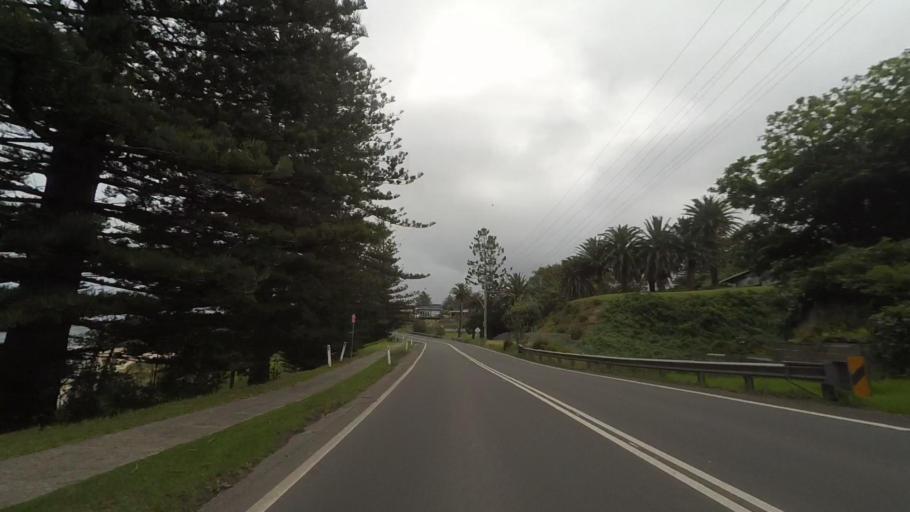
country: AU
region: New South Wales
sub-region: Wollongong
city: Bulli
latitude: -34.3034
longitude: 150.9375
